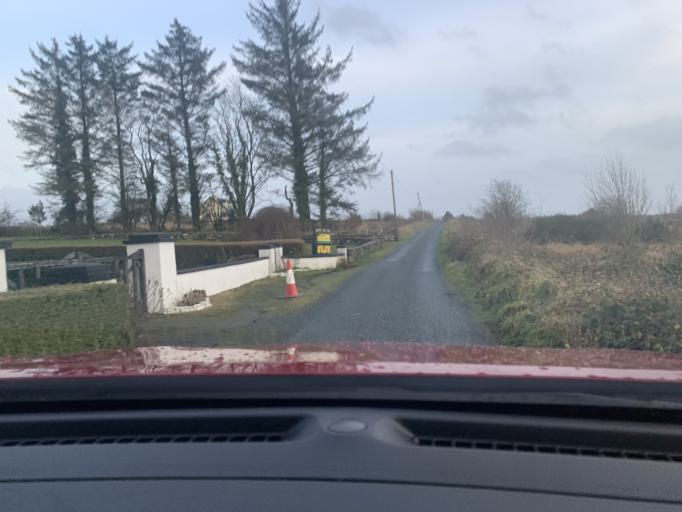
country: IE
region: Connaught
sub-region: Roscommon
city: Ballaghaderreen
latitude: 53.9569
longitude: -8.5336
